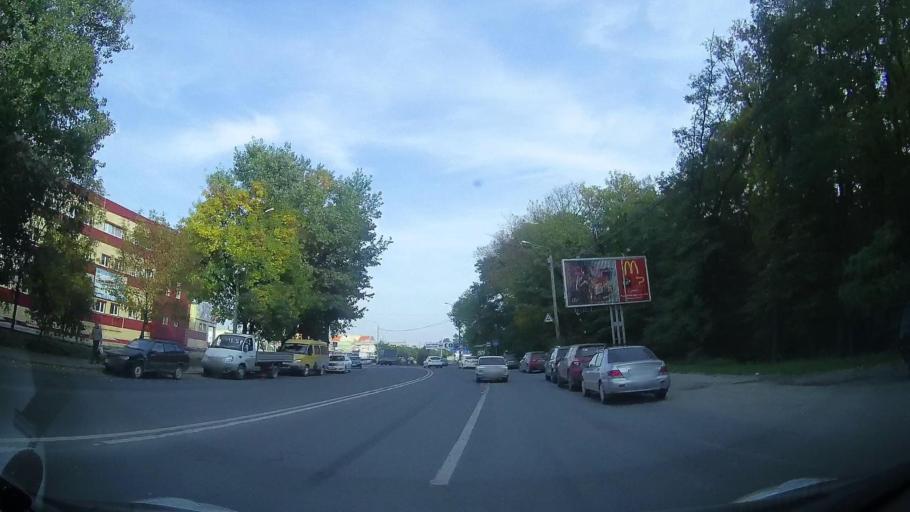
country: RU
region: Rostov
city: Aksay
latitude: 47.2746
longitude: 39.8146
